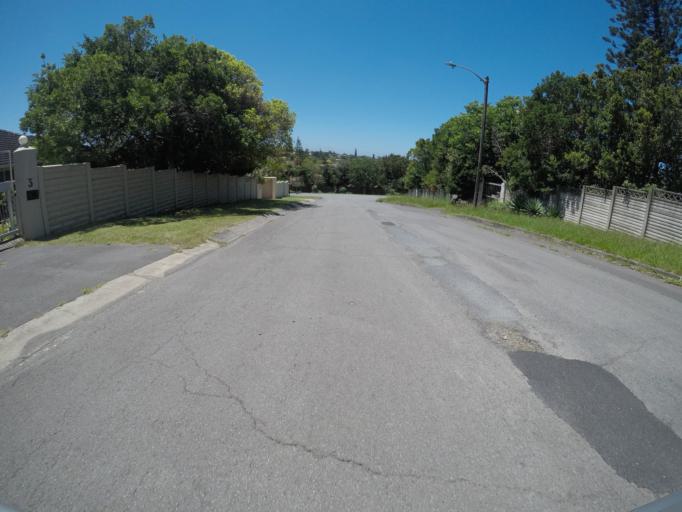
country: ZA
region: Eastern Cape
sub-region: Buffalo City Metropolitan Municipality
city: East London
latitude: -32.9642
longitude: 27.9361
